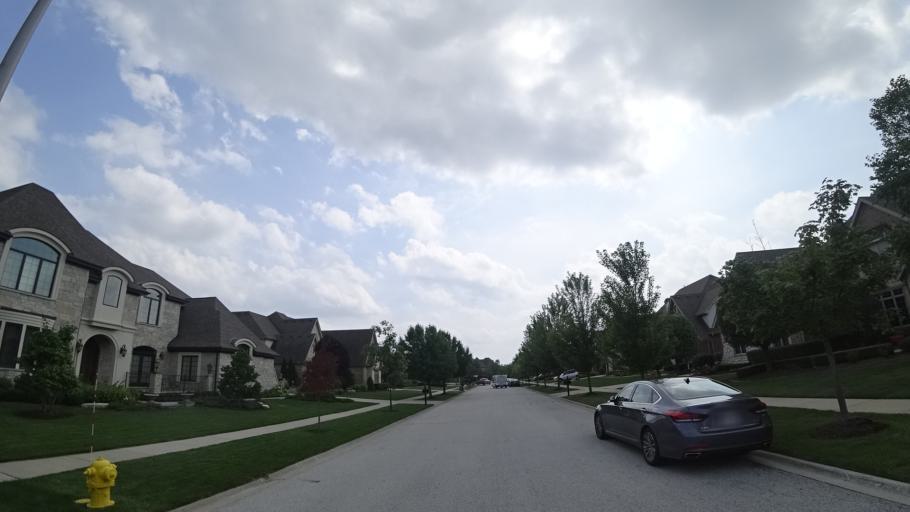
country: US
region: Illinois
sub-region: Cook County
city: Orland Park
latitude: 41.6355
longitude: -87.8895
